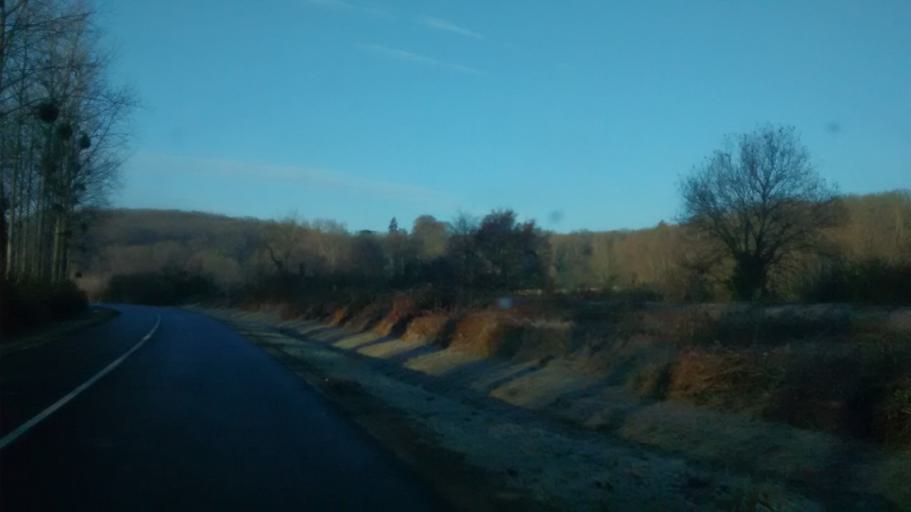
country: FR
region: Centre
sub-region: Departement d'Indre-et-Loire
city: Veigne
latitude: 47.2937
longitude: 0.7419
